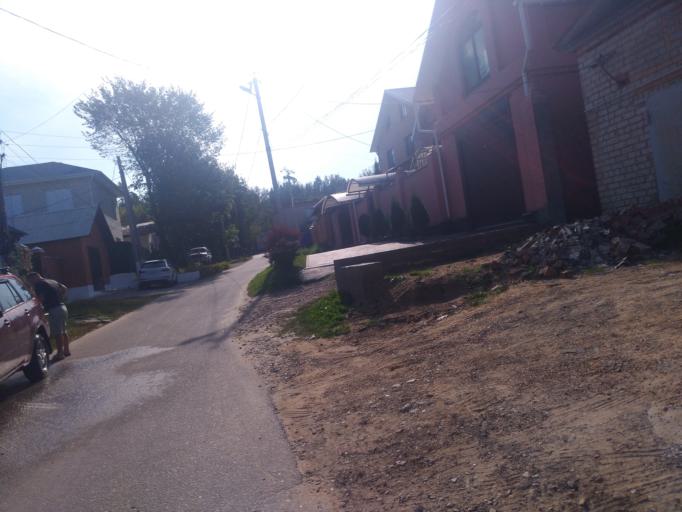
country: RU
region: Kaluga
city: Kaluga
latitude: 54.5360
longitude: 36.2516
